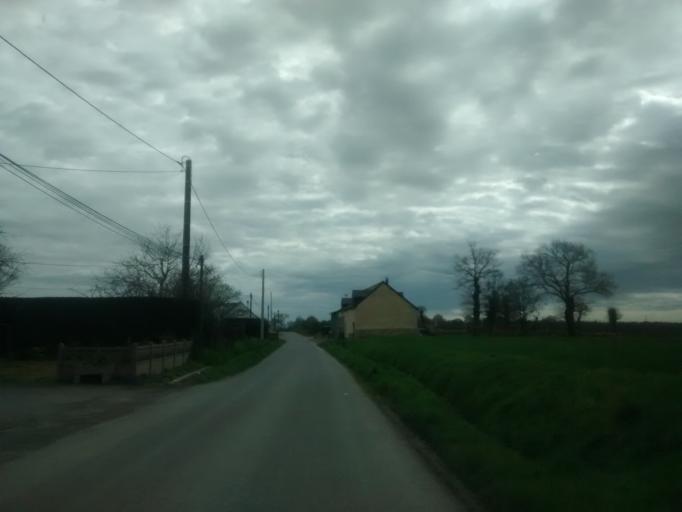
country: FR
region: Brittany
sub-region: Departement d'Ille-et-Vilaine
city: Erce-pres-Liffre
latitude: 48.2443
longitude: -1.5198
